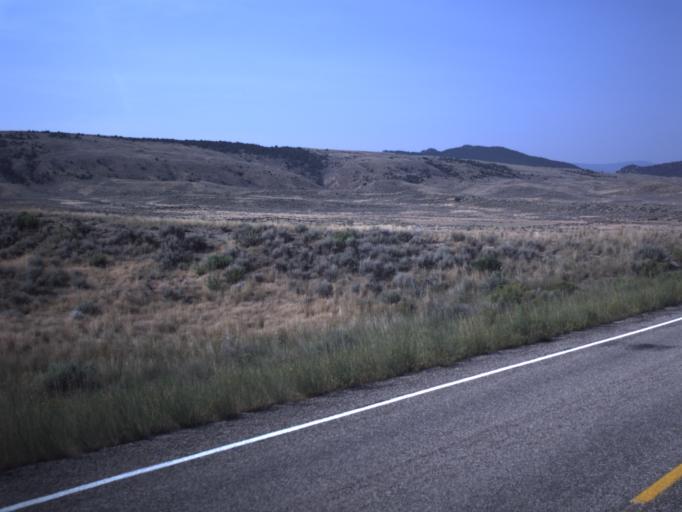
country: US
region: Utah
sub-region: Daggett County
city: Manila
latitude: 40.9832
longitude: -109.4449
